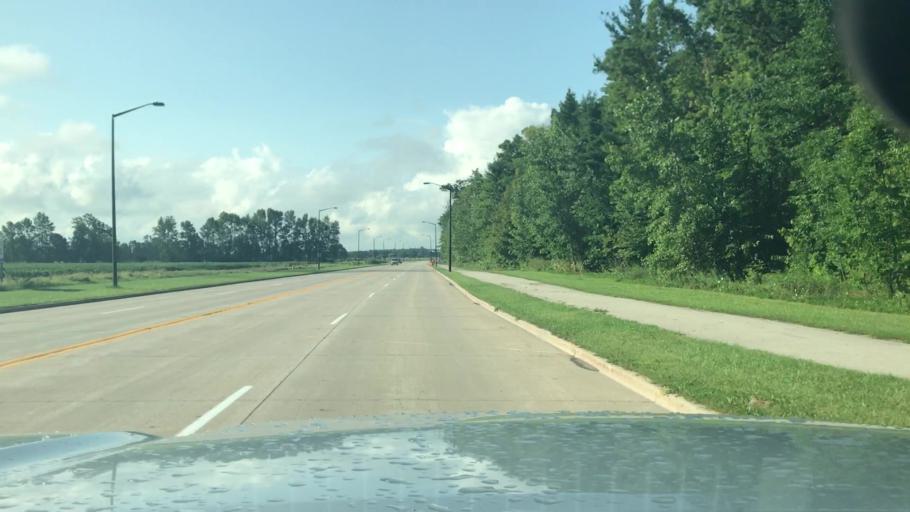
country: US
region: Wisconsin
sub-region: Brown County
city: Bellevue
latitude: 44.4762
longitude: -87.9173
